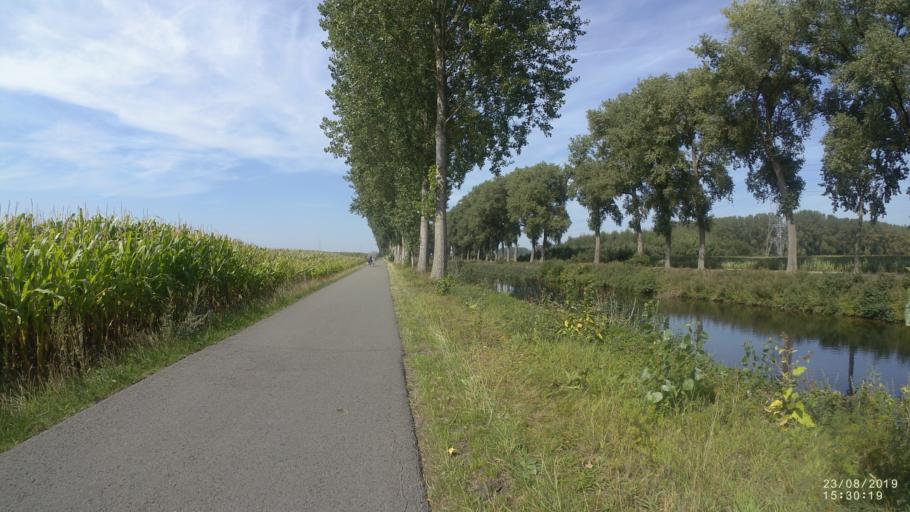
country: BE
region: Flanders
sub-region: Provincie Oost-Vlaanderen
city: Zomergem
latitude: 51.1486
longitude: 3.5533
